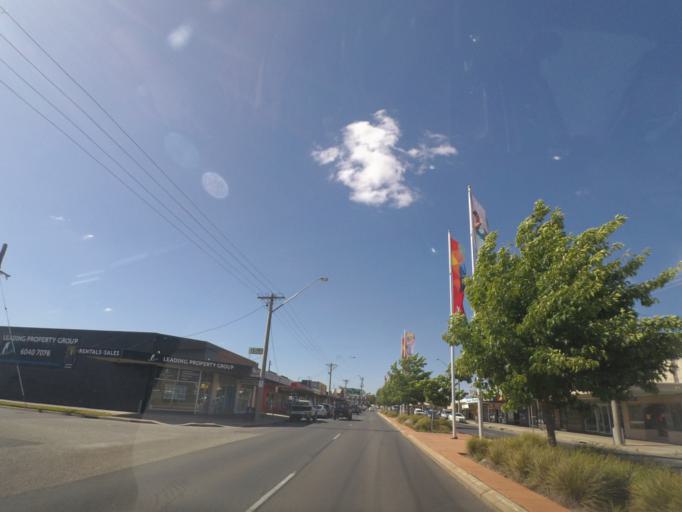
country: AU
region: New South Wales
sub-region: Albury Municipality
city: North Albury
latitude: -36.0545
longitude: 146.9332
